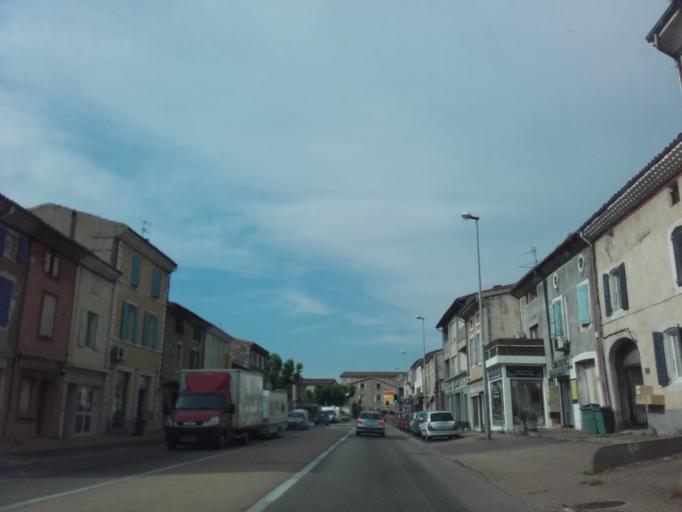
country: FR
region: Rhone-Alpes
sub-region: Departement de la Drome
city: Livron-sur-Drome
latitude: 44.7704
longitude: 4.8419
